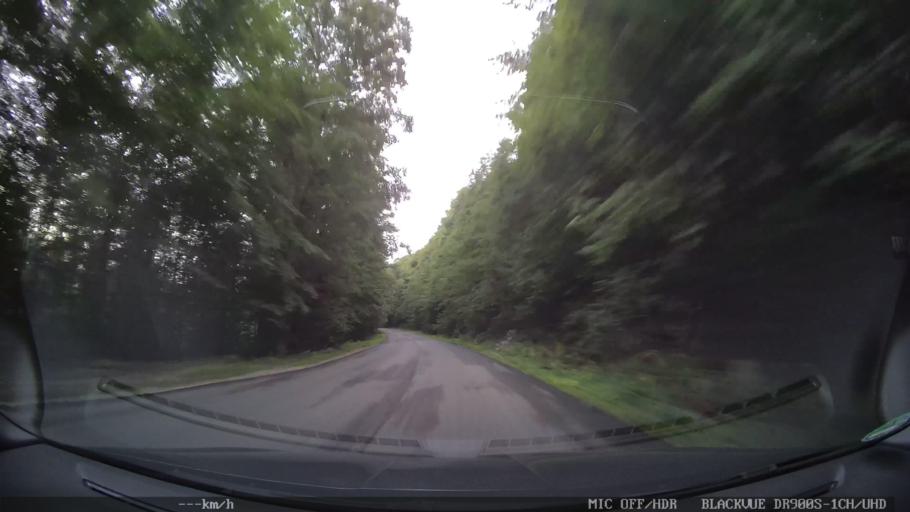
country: HR
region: Primorsko-Goranska
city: Vrbovsko
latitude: 45.1856
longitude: 14.9890
